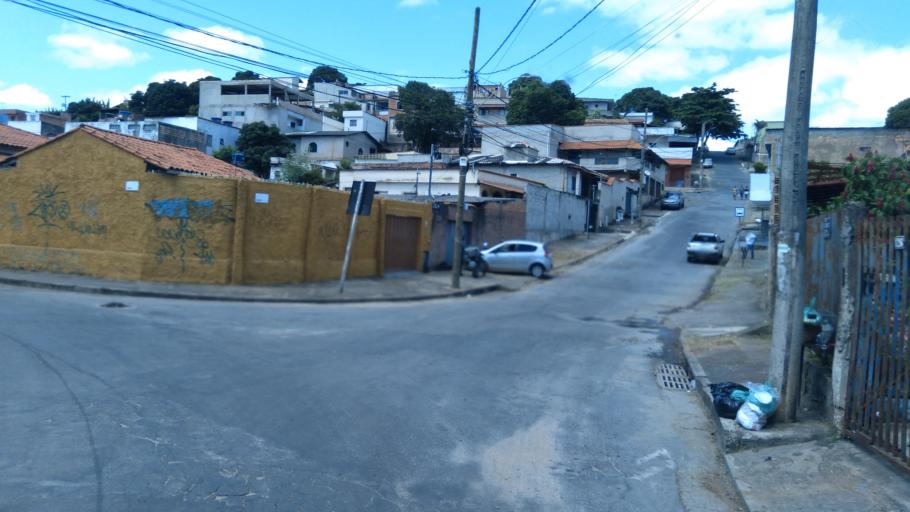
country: BR
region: Minas Gerais
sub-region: Belo Horizonte
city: Belo Horizonte
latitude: -19.8614
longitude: -43.9059
